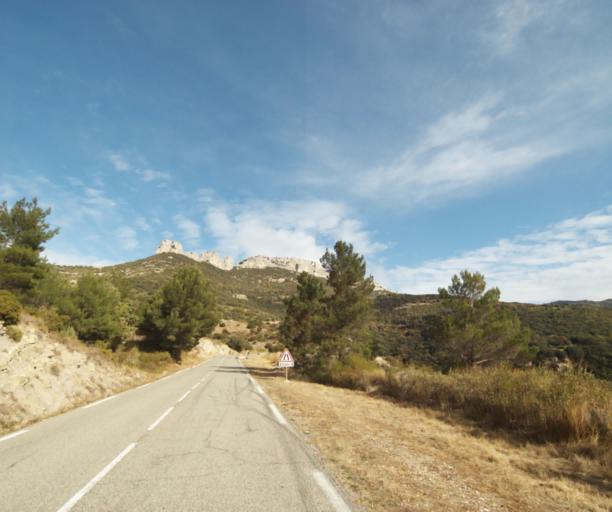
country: FR
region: Provence-Alpes-Cote d'Azur
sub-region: Departement des Bouches-du-Rhone
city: Gemenos
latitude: 43.3104
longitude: 5.6648
